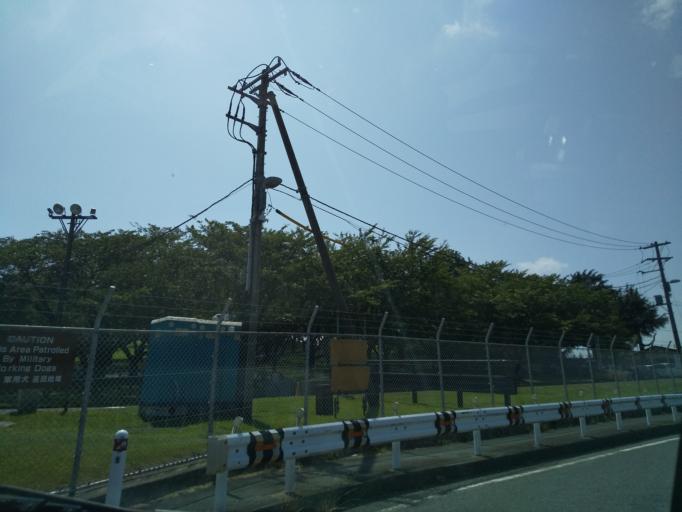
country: JP
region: Kanagawa
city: Zama
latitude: 35.5121
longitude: 139.3985
